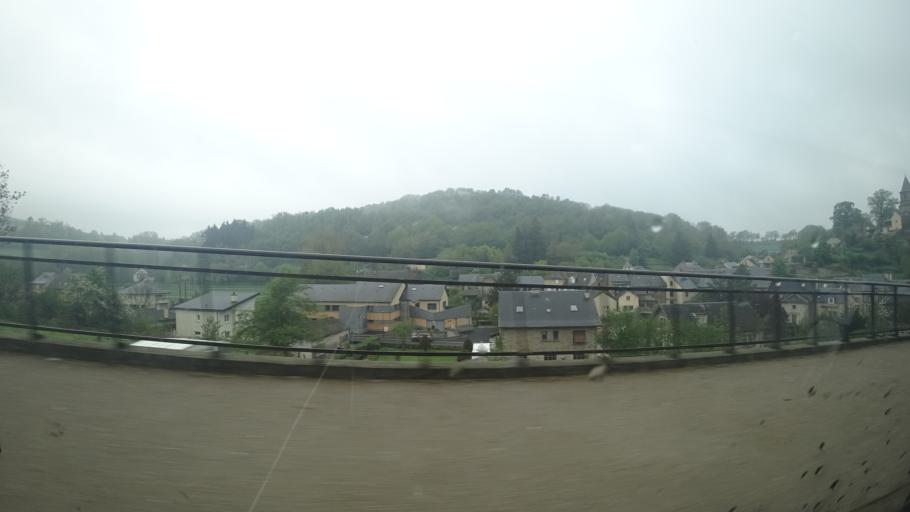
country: FR
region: Midi-Pyrenees
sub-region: Departement de l'Aveyron
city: Laissac
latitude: 44.2920
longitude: 2.8354
